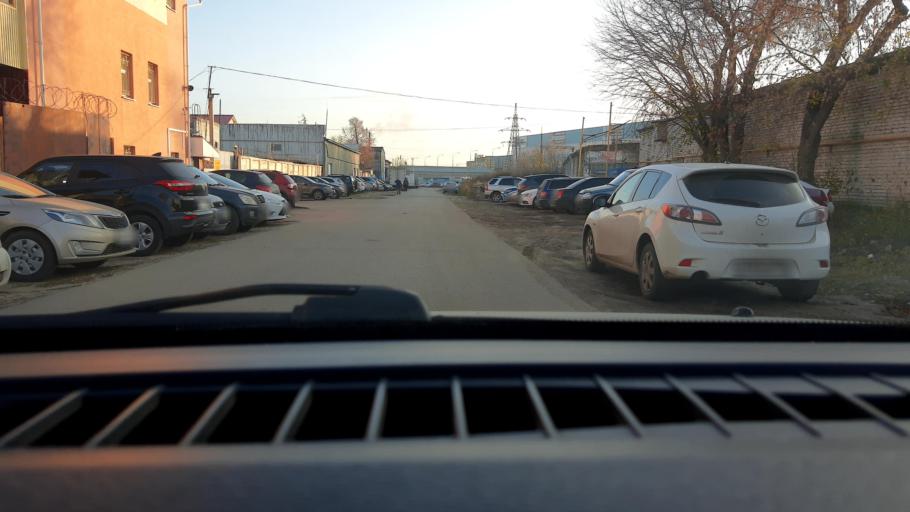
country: RU
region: Nizjnij Novgorod
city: Gorbatovka
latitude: 56.3076
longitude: 43.8658
